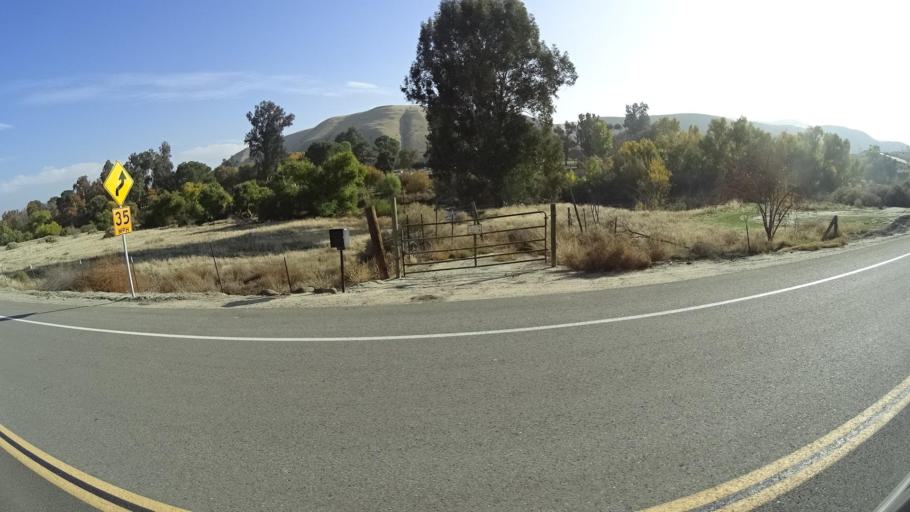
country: US
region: California
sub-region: Kern County
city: Oildale
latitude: 35.4510
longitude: -118.9168
